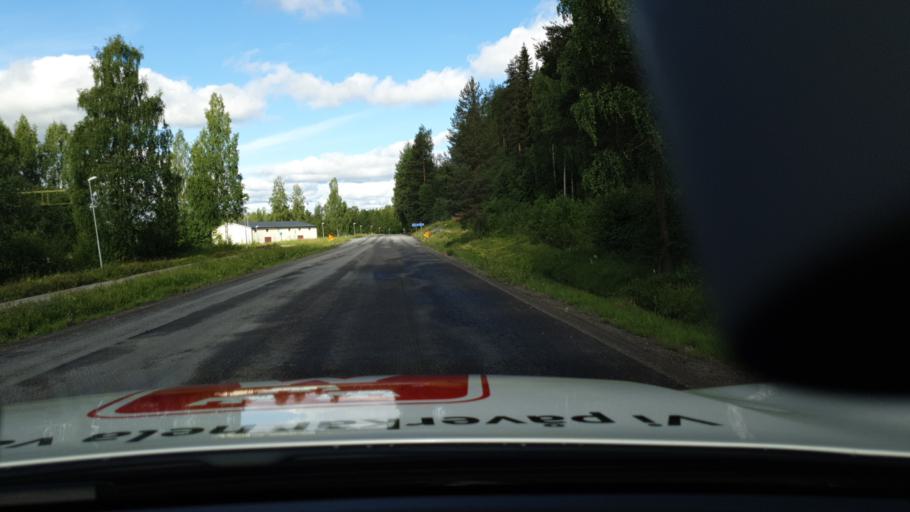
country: SE
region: Norrbotten
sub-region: Bodens Kommun
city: Boden
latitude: 65.8299
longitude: 21.6321
